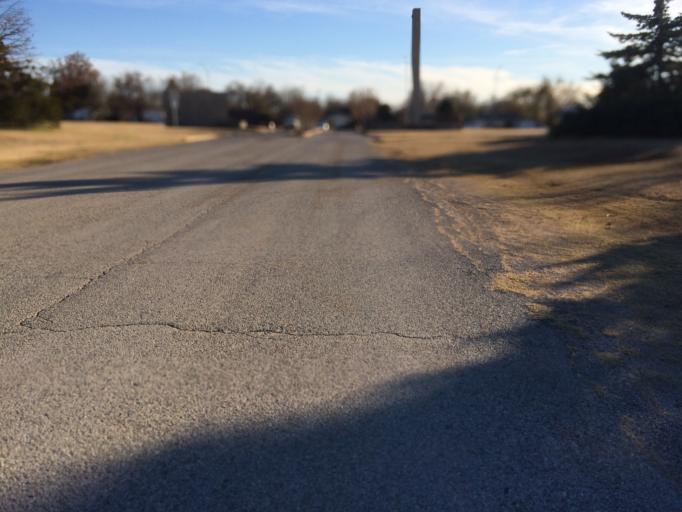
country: US
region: Oklahoma
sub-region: Cleveland County
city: Norman
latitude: 35.2340
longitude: -97.4554
